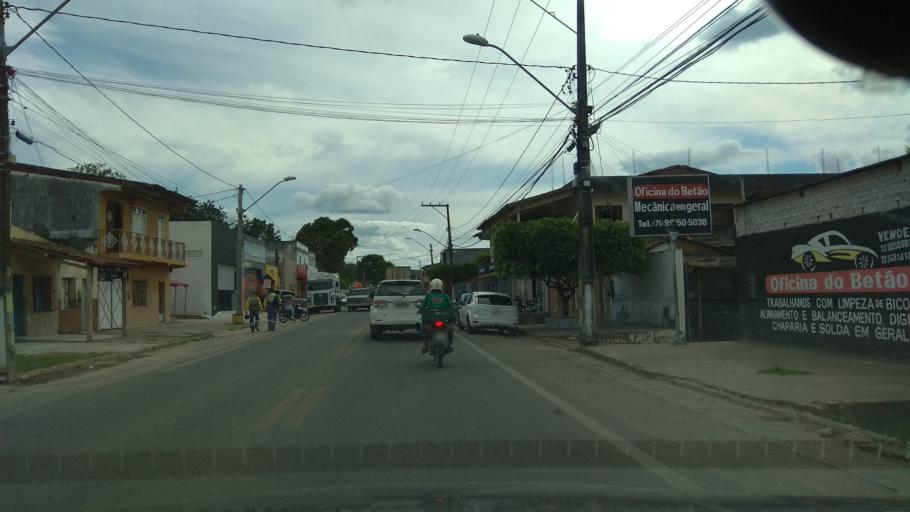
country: BR
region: Bahia
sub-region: Ipiau
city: Ipiau
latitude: -14.1345
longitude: -39.7479
